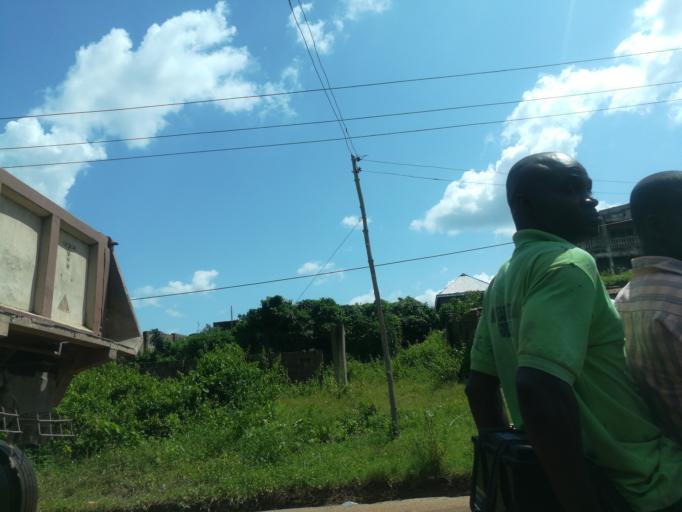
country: NG
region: Oyo
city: Lalupon
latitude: 7.4421
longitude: 4.0104
